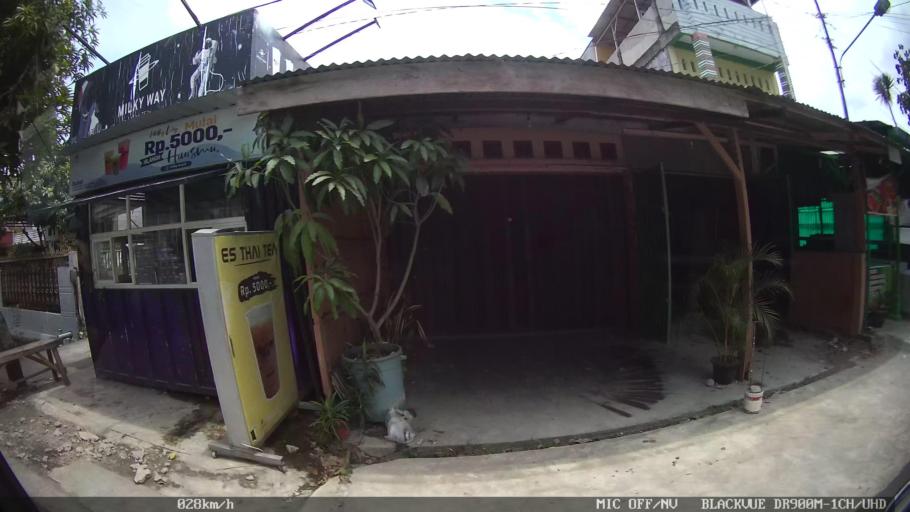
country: ID
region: North Sumatra
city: Medan
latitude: 3.5550
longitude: 98.6604
